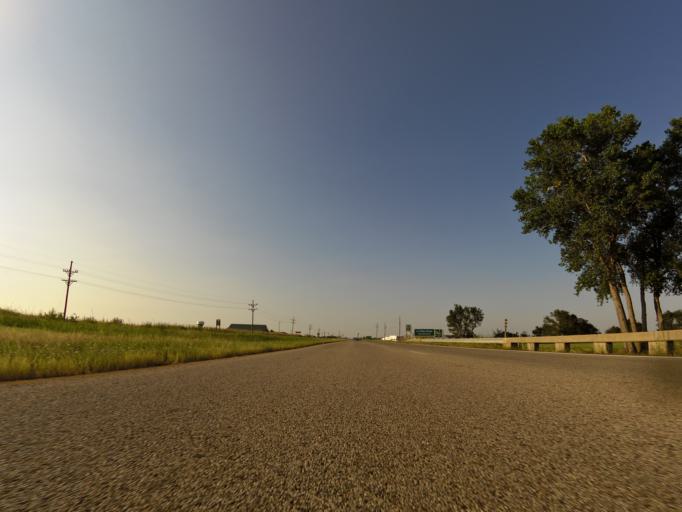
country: US
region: Kansas
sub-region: Reno County
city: South Hutchinson
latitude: 38.0038
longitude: -97.9403
